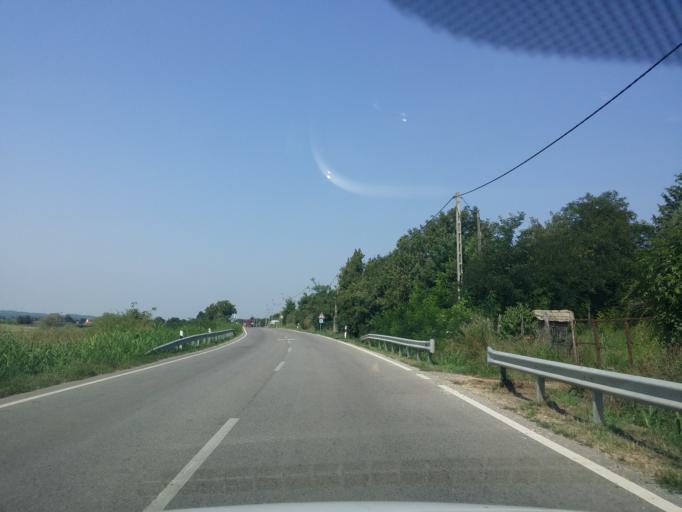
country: HU
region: Tolna
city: Pincehely
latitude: 46.7051
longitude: 18.4701
